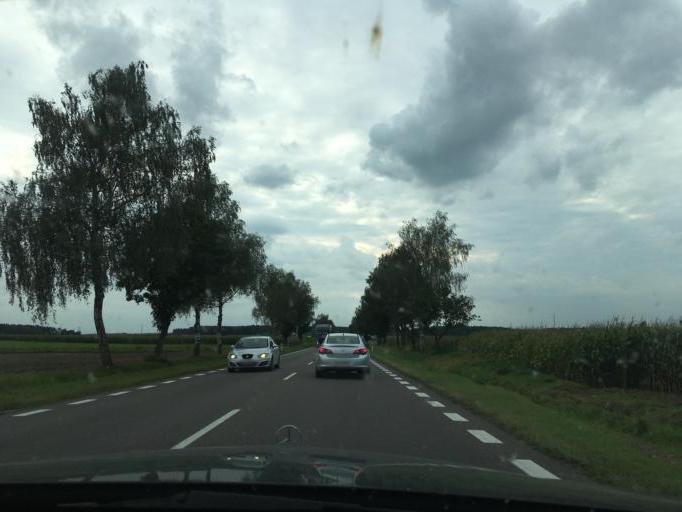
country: PL
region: Podlasie
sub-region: Powiat grajewski
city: Szczuczyn
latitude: 53.6003
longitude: 22.3583
